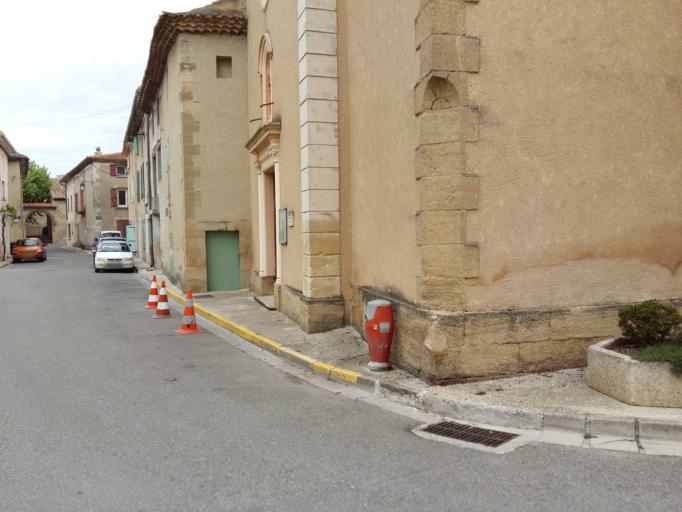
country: FR
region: Provence-Alpes-Cote d'Azur
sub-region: Departement du Vaucluse
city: Violes
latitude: 44.1612
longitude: 4.9561
